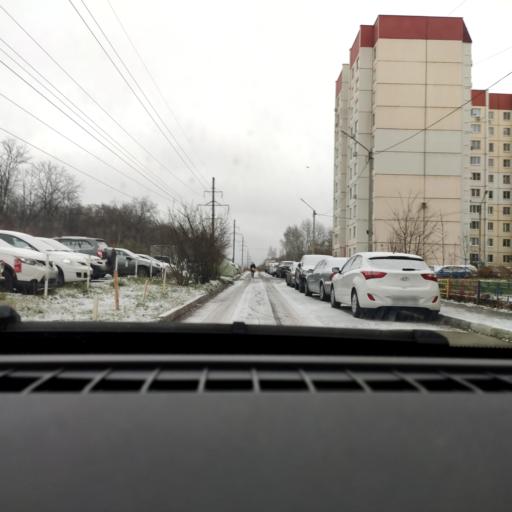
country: RU
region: Voronezj
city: Podgornoye
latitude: 51.7319
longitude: 39.2037
